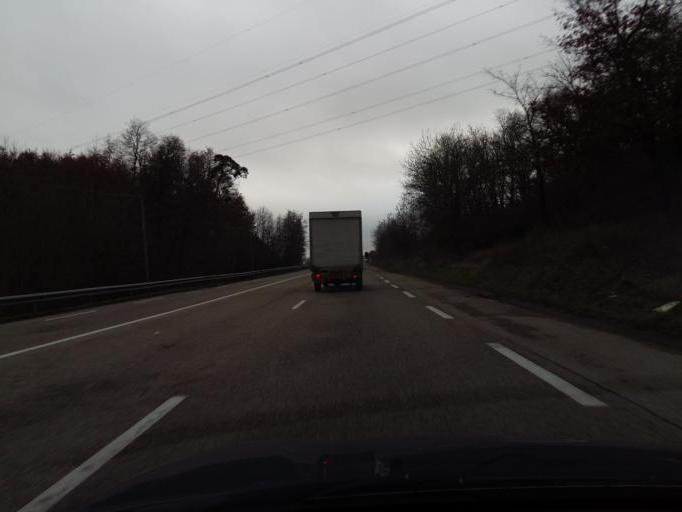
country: FR
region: Rhone-Alpes
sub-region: Departement de l'Ardeche
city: Saint-Cyr
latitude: 45.2494
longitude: 4.7518
